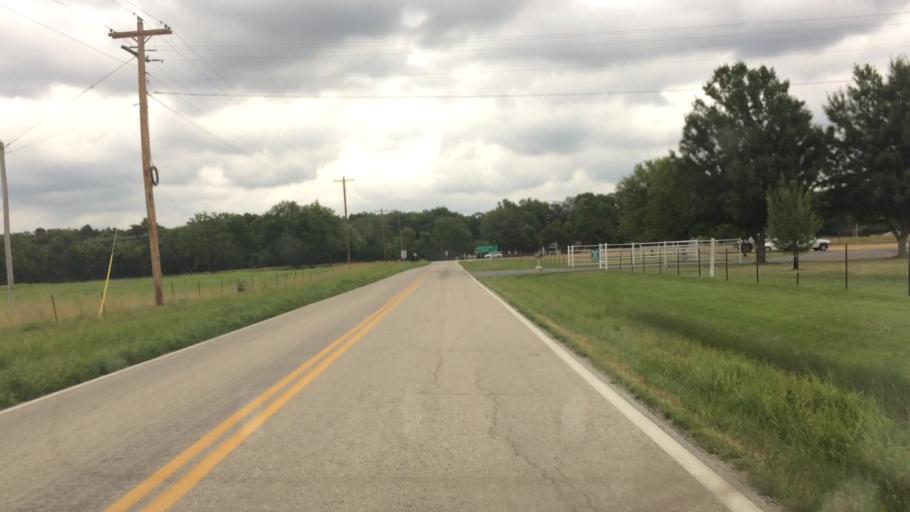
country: US
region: Missouri
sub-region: Greene County
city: Strafford
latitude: 37.2959
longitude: -93.1156
